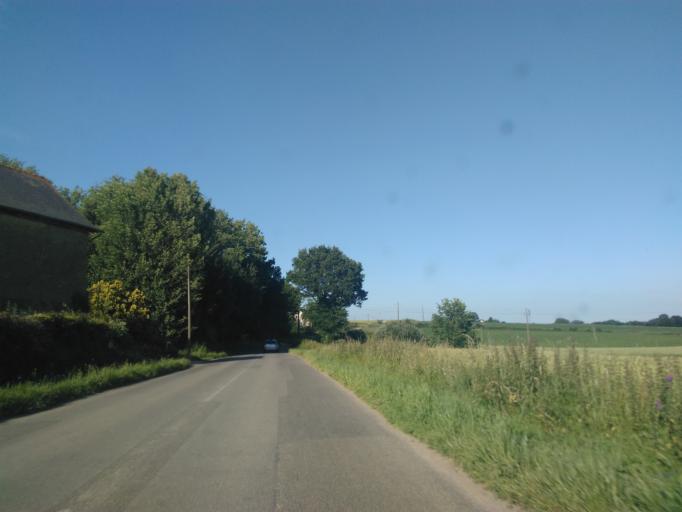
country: FR
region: Brittany
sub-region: Departement d'Ille-et-Vilaine
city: Geveze
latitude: 48.2191
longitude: -1.8177
